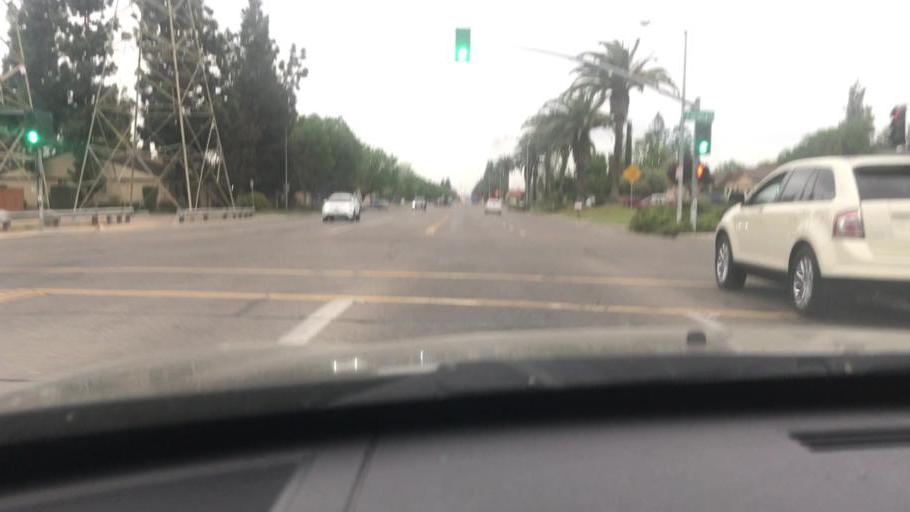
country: US
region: California
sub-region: Fresno County
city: West Park
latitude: 36.8145
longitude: -119.8707
